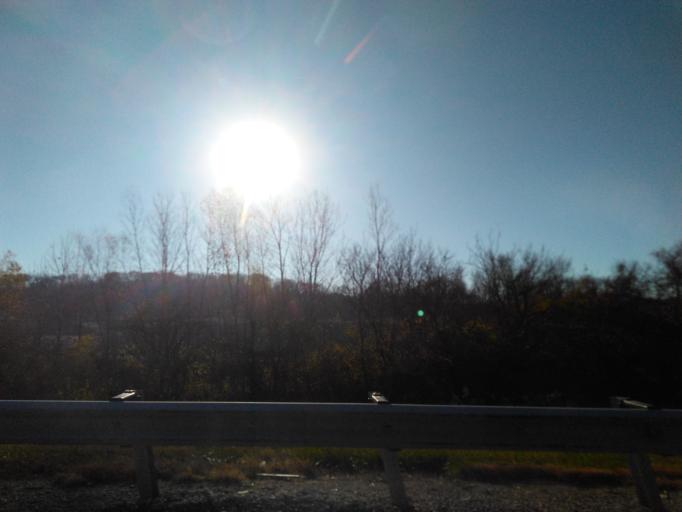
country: US
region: Illinois
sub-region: Saint Clair County
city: Cahokia
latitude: 38.5424
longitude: -90.1757
